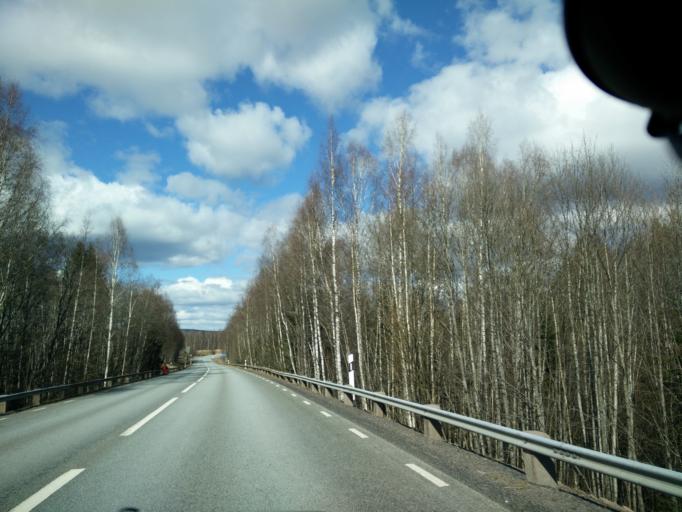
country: SE
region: Vaermland
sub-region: Munkfors Kommun
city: Munkfors
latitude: 59.8577
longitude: 13.5622
